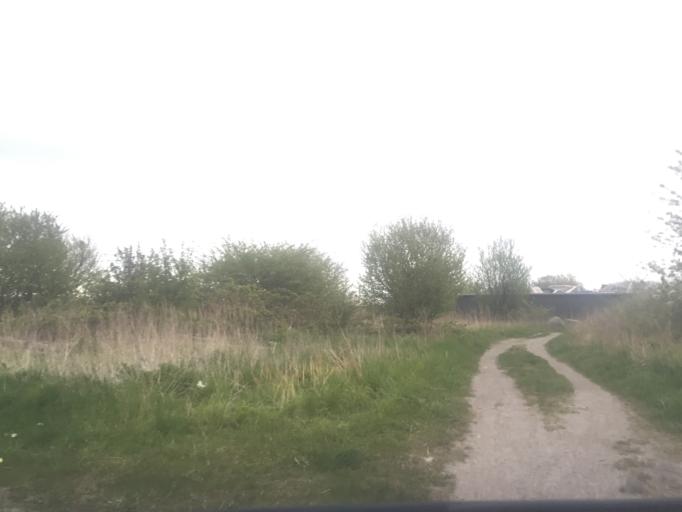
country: DK
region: Capital Region
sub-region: Frederiksberg Kommune
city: Frederiksberg
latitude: 55.6399
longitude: 12.5446
